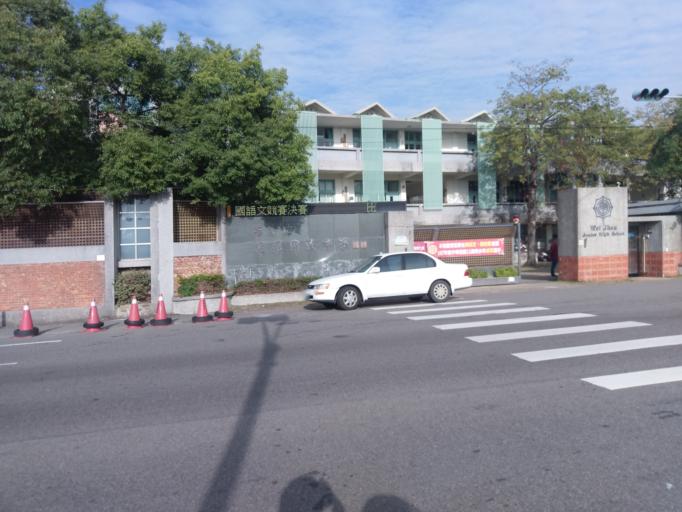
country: TW
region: Taiwan
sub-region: Miaoli
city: Miaoli
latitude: 24.6121
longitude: 120.7944
